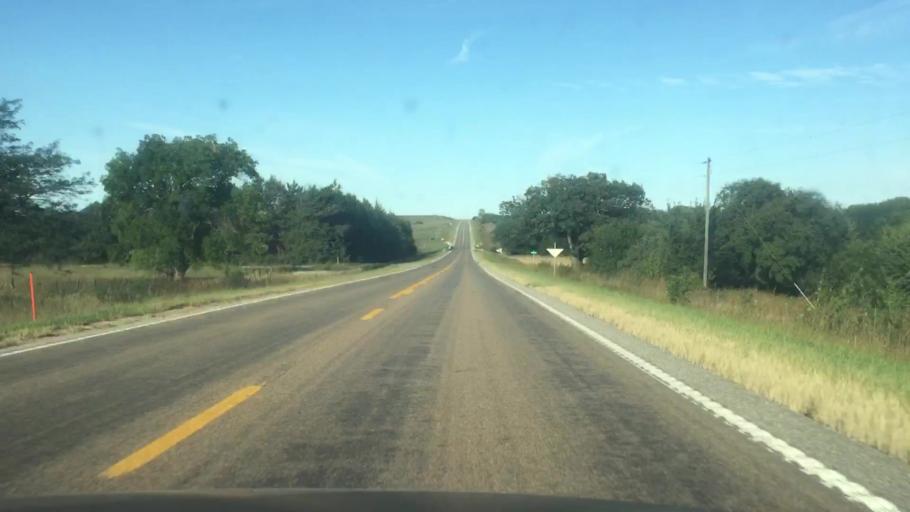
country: US
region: Nebraska
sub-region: Thayer County
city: Hebron
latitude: 40.1472
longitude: -97.5187
